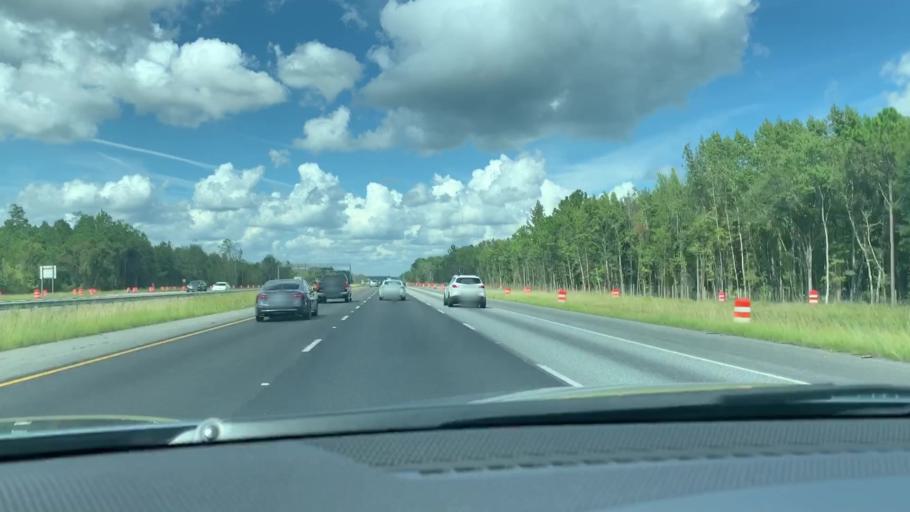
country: US
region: Georgia
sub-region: Camden County
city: Kingsland
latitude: 30.8491
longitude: -81.6731
